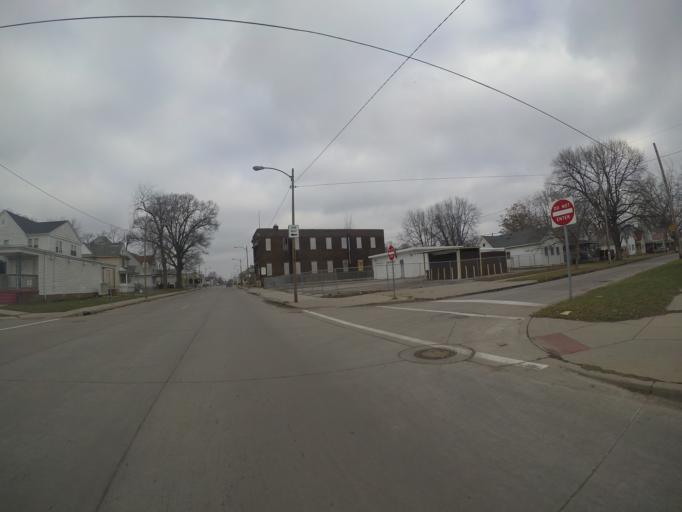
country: US
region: Ohio
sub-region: Lucas County
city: Oregon
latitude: 41.6405
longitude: -83.5158
